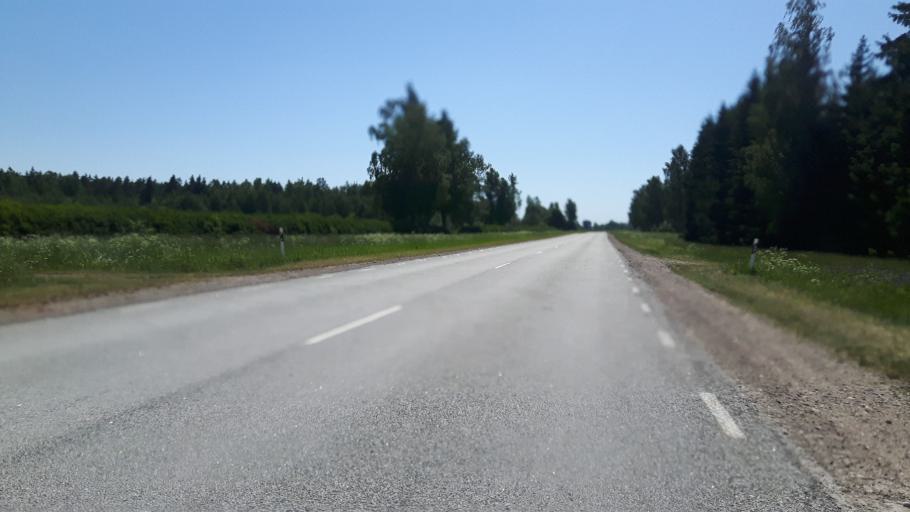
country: EE
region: Paernumaa
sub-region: Tootsi vald
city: Tootsi
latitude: 58.4589
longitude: 24.7803
